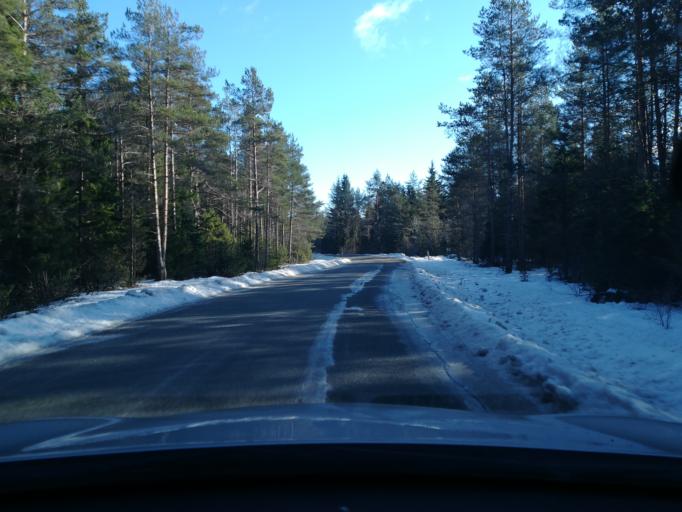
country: EE
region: Harju
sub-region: Kiili vald
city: Kiili
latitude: 59.2649
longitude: 24.8064
